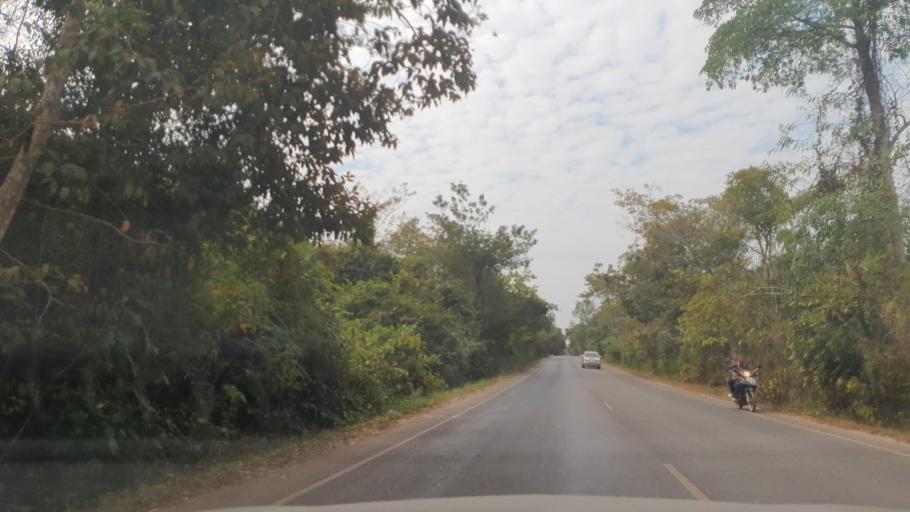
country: TH
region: Changwat Bueng Kan
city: Bung Khla
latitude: 18.3029
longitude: 103.9577
